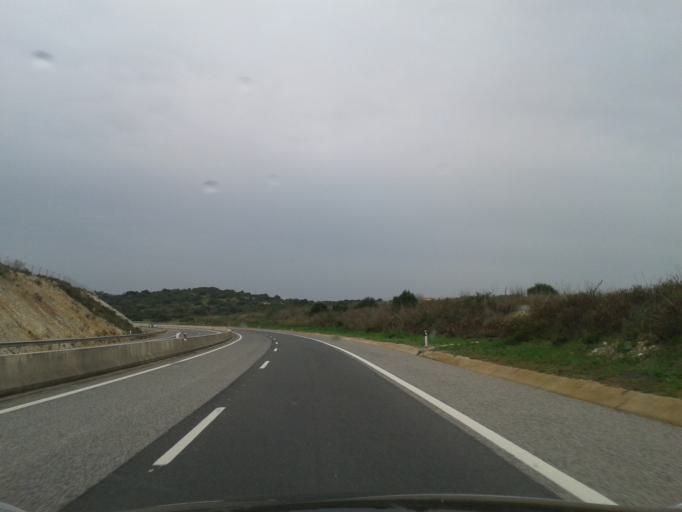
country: PT
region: Faro
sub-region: Lagos
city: Lagos
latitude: 37.1308
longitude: -8.7115
